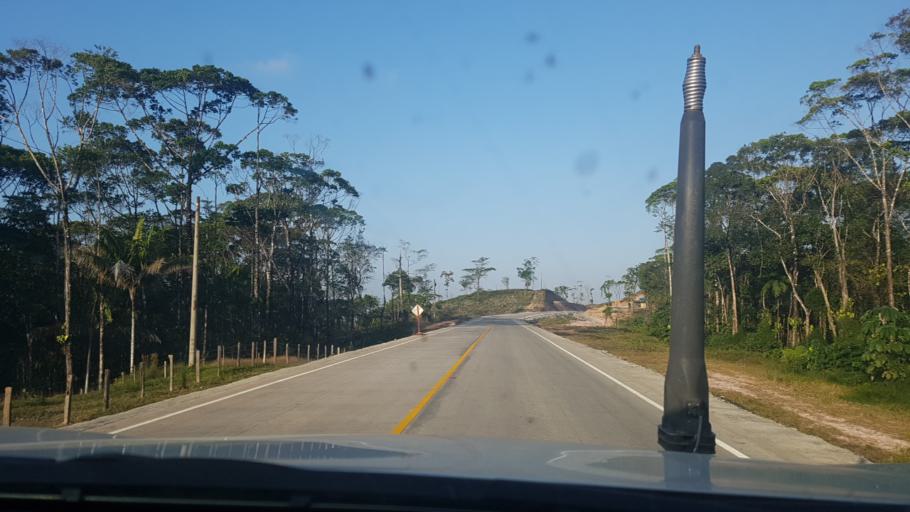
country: NI
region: Atlantico Sur
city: Rama
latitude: 11.8325
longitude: -84.0793
